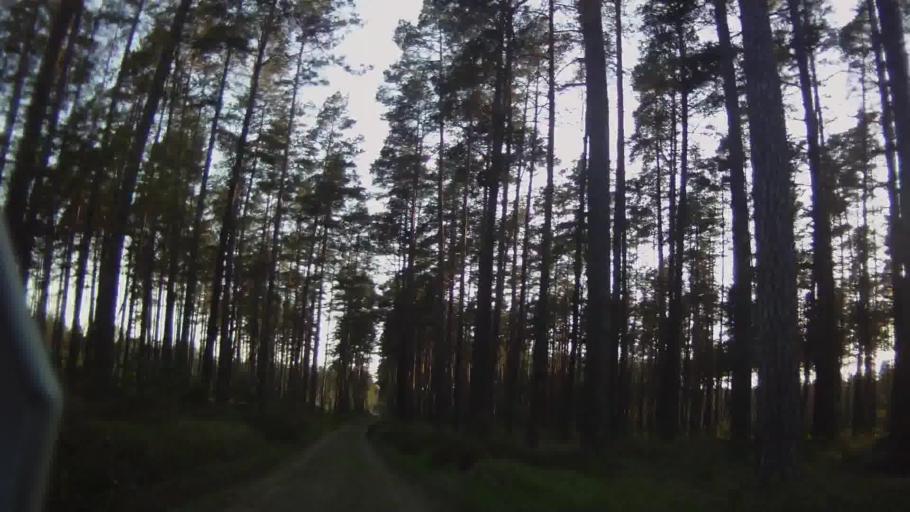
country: LV
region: Riga
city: Jaunciems
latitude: 57.0670
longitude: 24.1762
